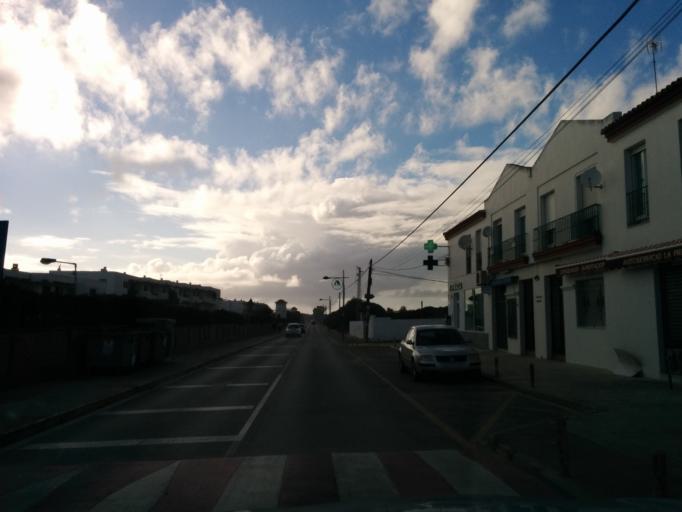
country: ES
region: Andalusia
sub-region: Provincia de Cadiz
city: Vejer de la Frontera
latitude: 36.1861
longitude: -6.0145
